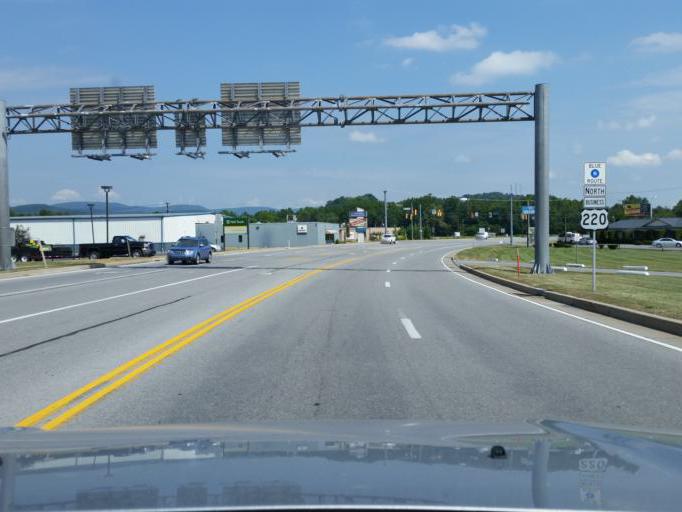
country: US
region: Pennsylvania
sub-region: Blair County
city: Duncansville
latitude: 40.4287
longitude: -78.4175
